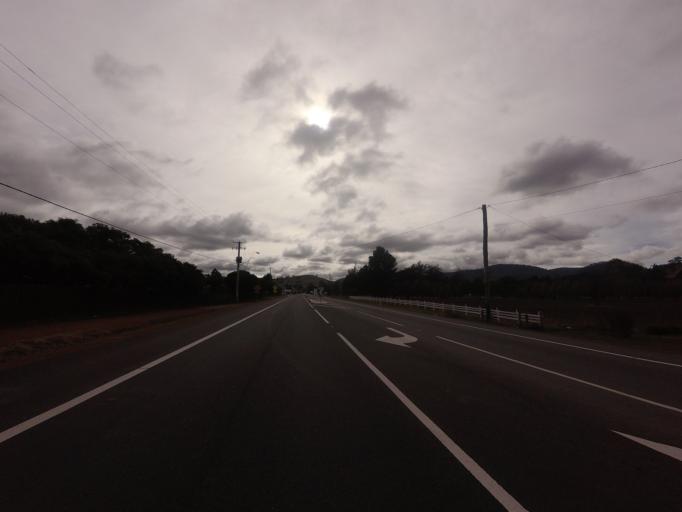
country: AU
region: Tasmania
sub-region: Brighton
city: Bridgewater
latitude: -42.6052
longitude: 147.2205
